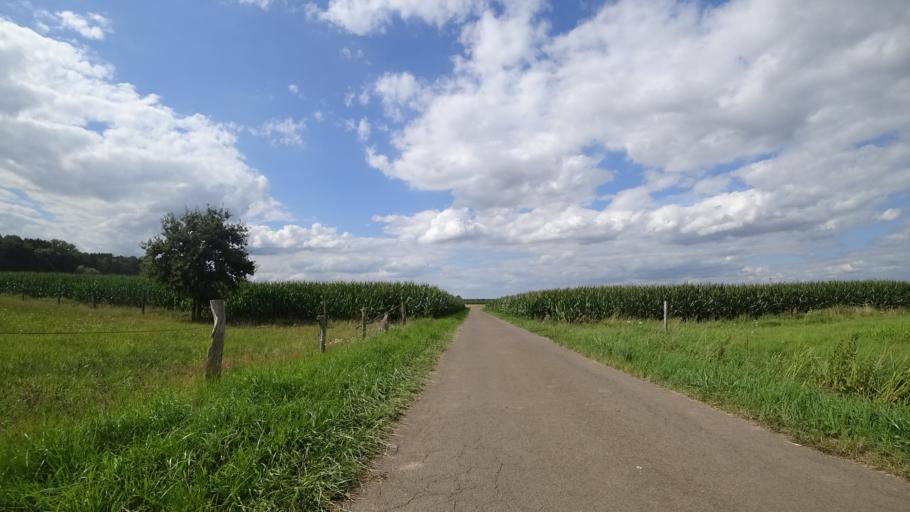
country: DE
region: Lower Saxony
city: Stolzenau
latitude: 52.4637
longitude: 9.0307
